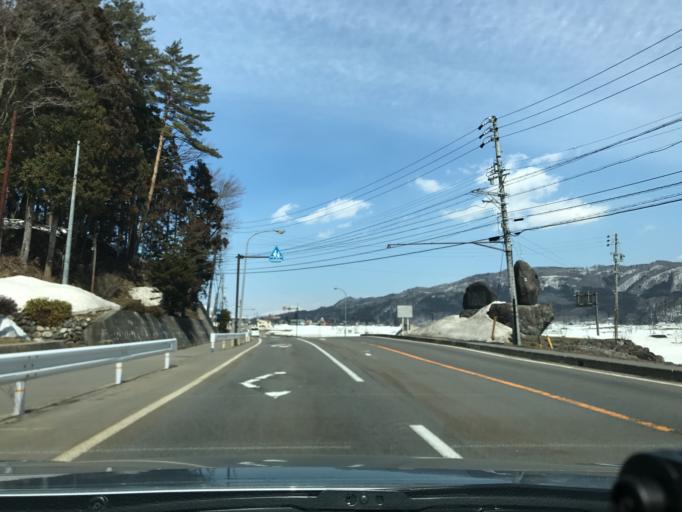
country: JP
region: Nagano
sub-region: Kitaazumi Gun
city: Hakuba
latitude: 36.6472
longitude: 137.8447
